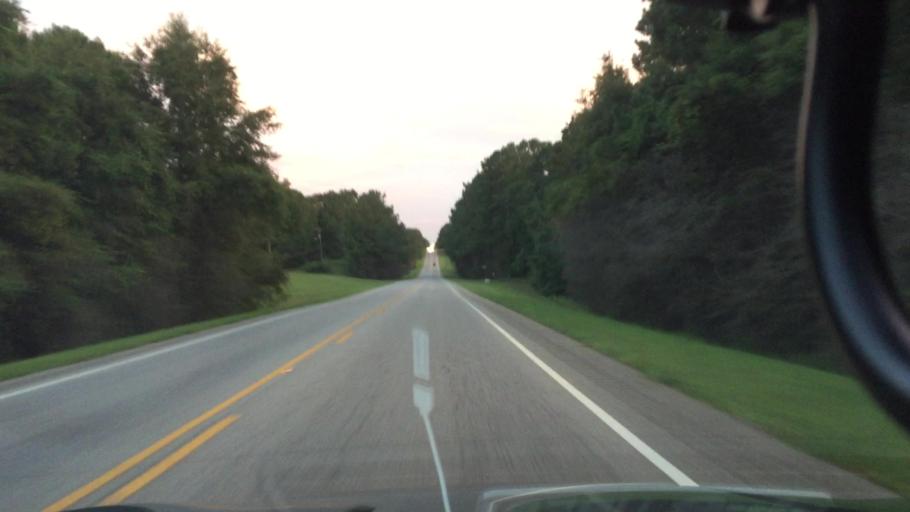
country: US
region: Alabama
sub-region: Coffee County
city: New Brockton
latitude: 31.3752
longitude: -85.8710
